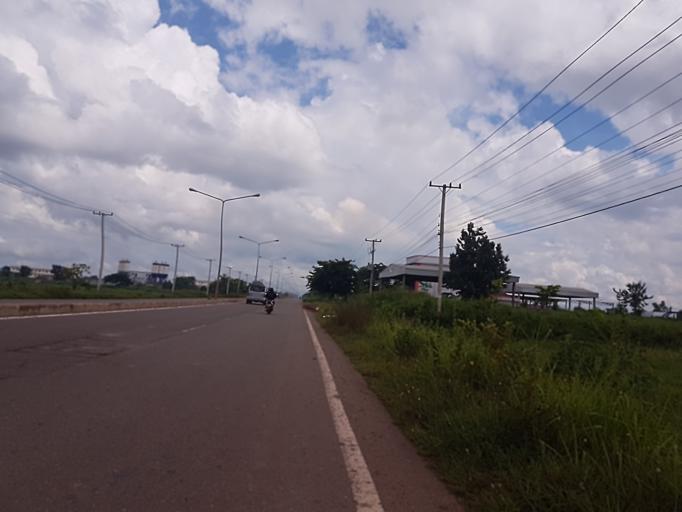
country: LA
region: Vientiane
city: Vientiane
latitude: 18.0112
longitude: 102.7224
